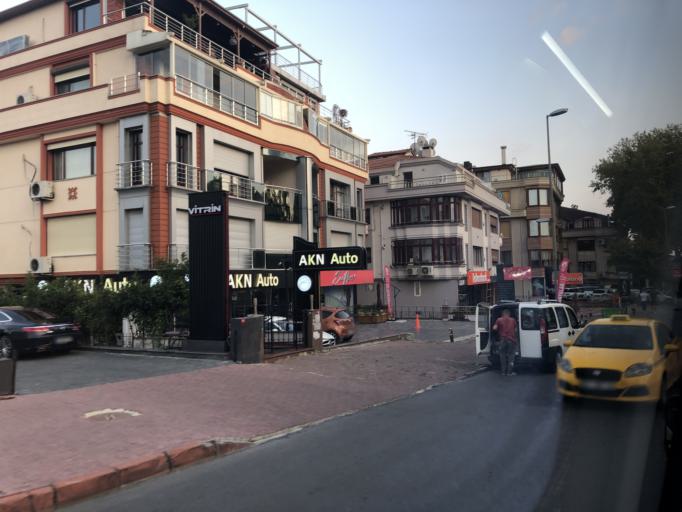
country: TR
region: Istanbul
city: Bahcelievler
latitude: 40.9777
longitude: 28.7918
